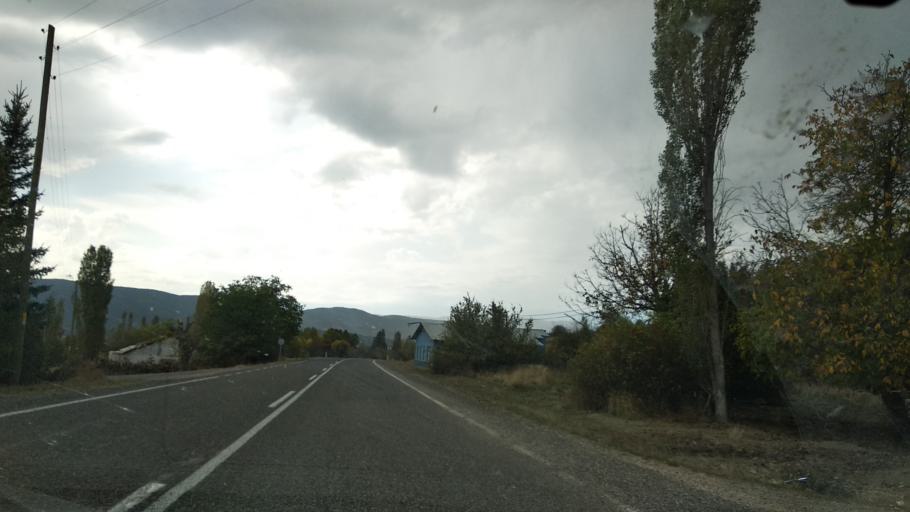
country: TR
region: Bolu
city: Seben
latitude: 40.3413
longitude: 31.4724
